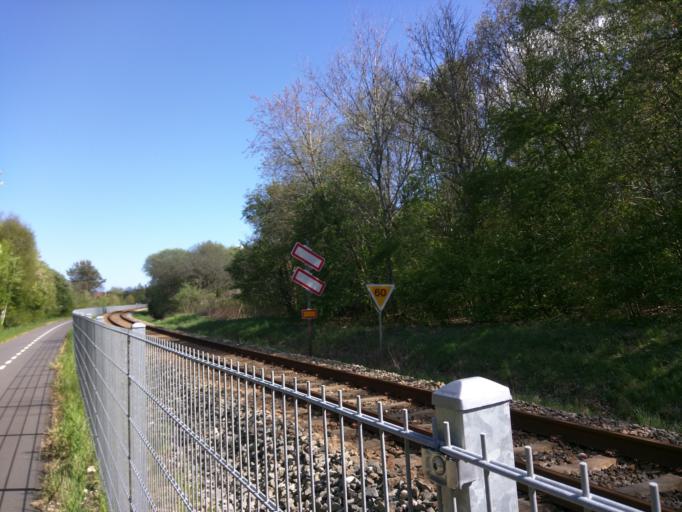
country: DK
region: Central Jutland
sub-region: Viborg Kommune
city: Viborg
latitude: 56.4552
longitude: 9.3747
